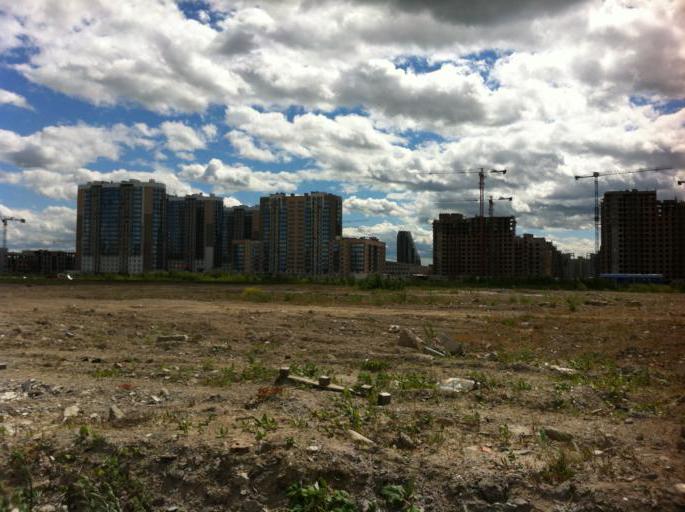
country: RU
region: St.-Petersburg
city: Sosnovaya Polyana
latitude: 59.8574
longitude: 30.1491
